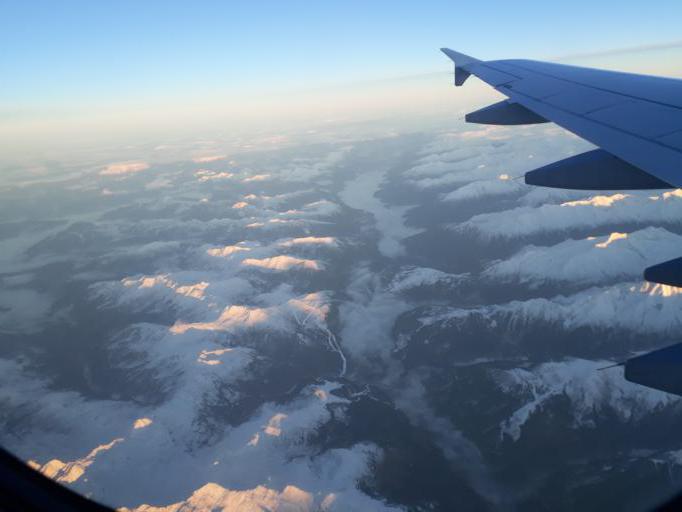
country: AT
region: Tyrol
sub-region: Politischer Bezirk Schwaz
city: Hainzenberg
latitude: 47.2165
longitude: 11.8968
